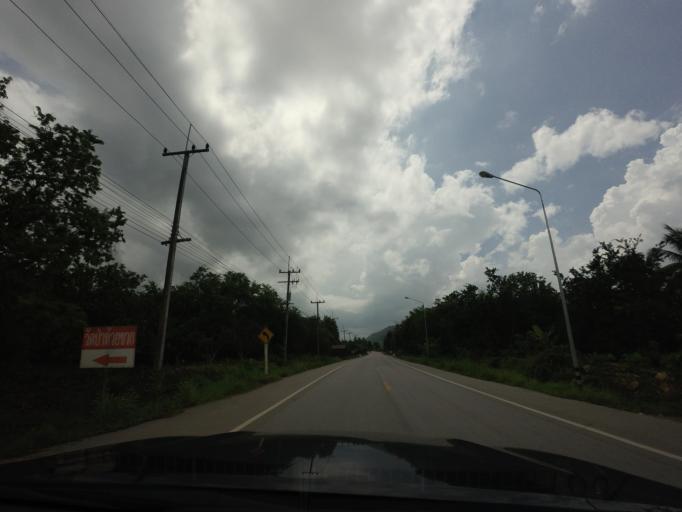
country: TH
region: Loei
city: Pak Chom
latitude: 18.0213
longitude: 101.7634
